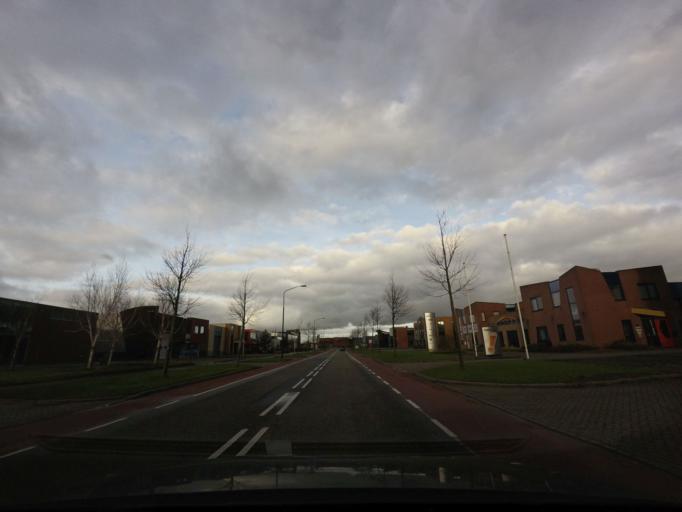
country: NL
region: North Holland
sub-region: Gemeente Heerhugowaard
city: Heerhugowaard
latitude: 52.6916
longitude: 4.8344
